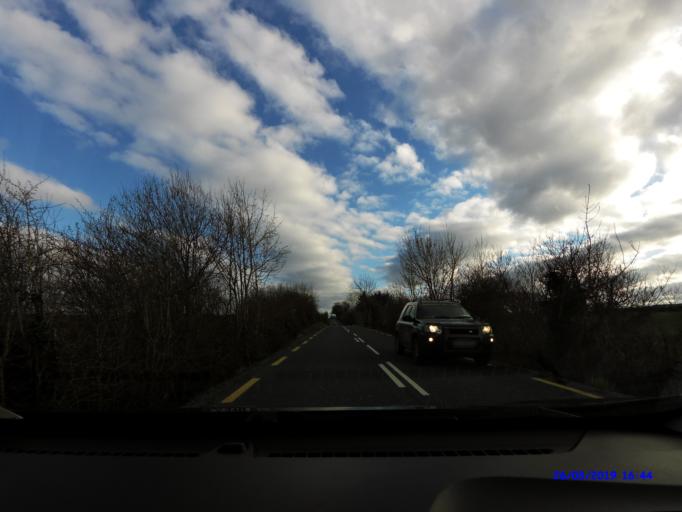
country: IE
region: Connaught
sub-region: Maigh Eo
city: Ballyhaunis
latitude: 53.8468
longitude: -8.7657
